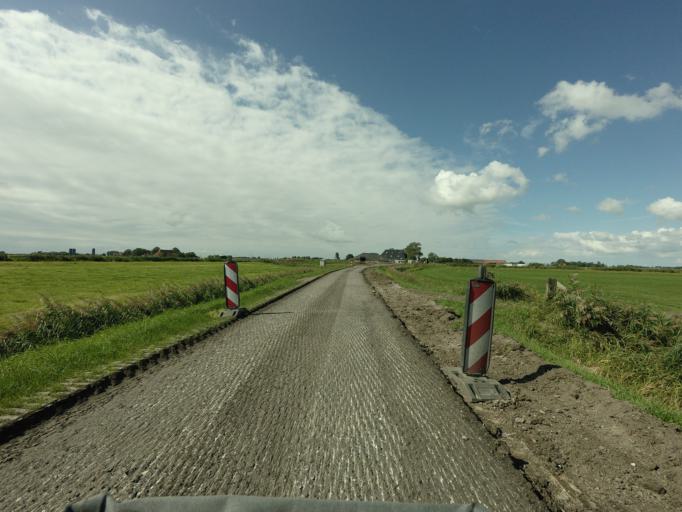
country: NL
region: Friesland
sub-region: Sudwest Fryslan
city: Bolsward
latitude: 53.0360
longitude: 5.5634
